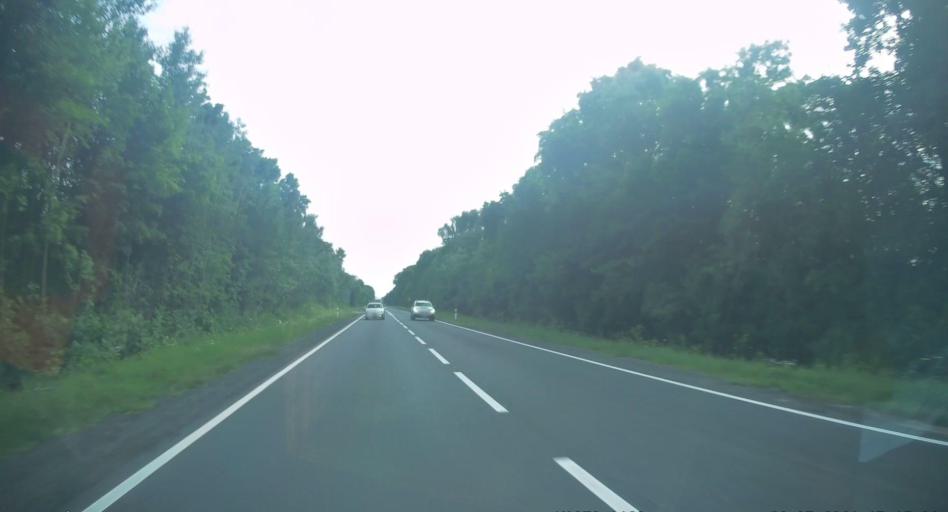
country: PL
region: Silesian Voivodeship
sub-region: Powiat czestochowski
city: Klomnice
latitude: 50.9432
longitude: 19.3915
